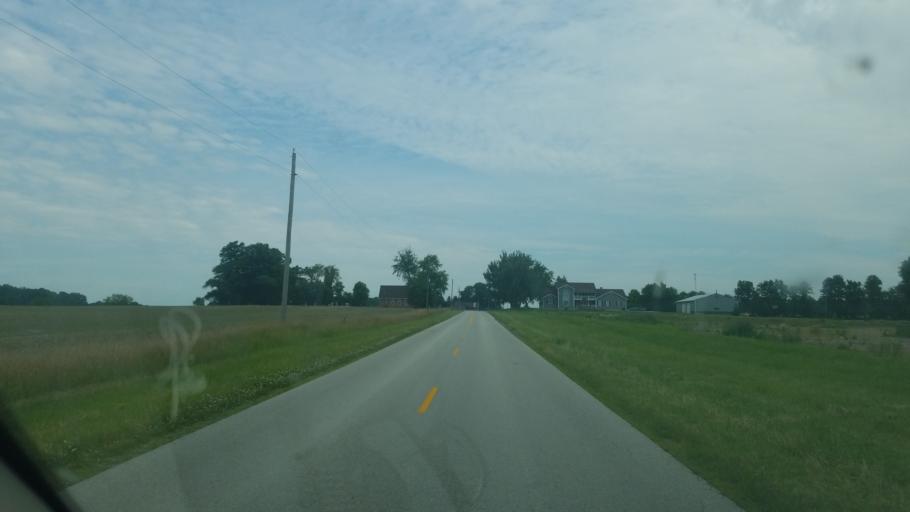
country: US
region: Ohio
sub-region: Wyandot County
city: Carey
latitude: 41.0333
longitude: -83.4398
